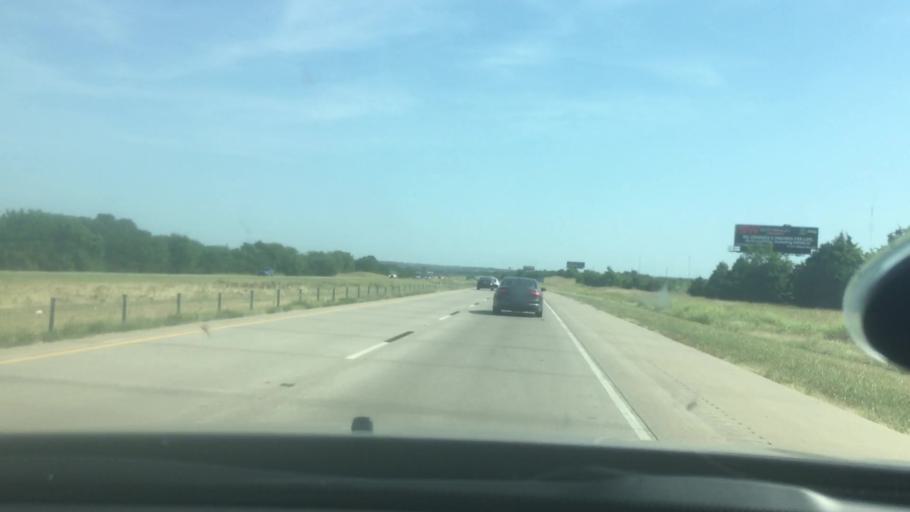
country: US
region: Oklahoma
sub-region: Carter County
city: Ardmore
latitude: 34.2865
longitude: -97.1594
